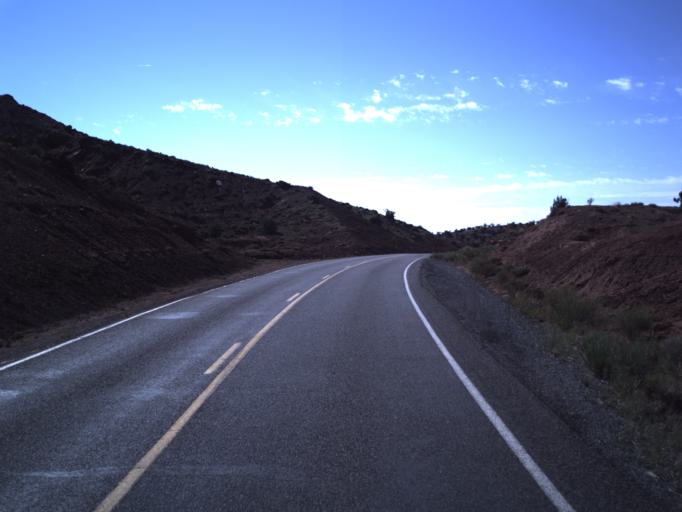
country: US
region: Utah
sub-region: Wayne County
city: Loa
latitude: 38.3121
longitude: -111.3004
